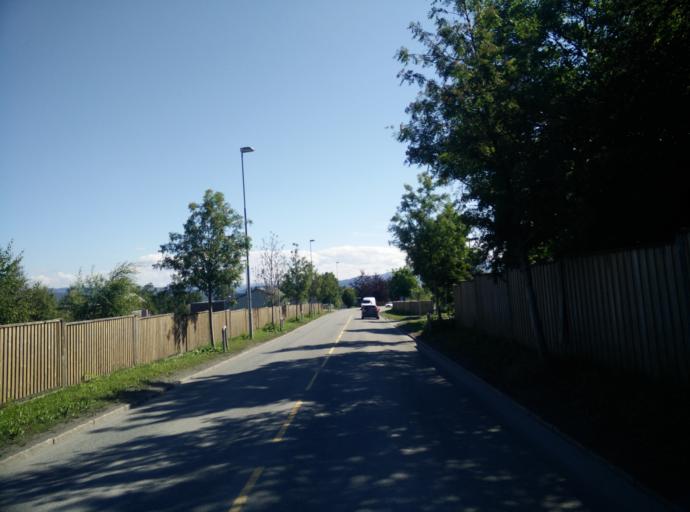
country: NO
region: Sor-Trondelag
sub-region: Trondheim
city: Trondheim
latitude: 63.4005
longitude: 10.3577
